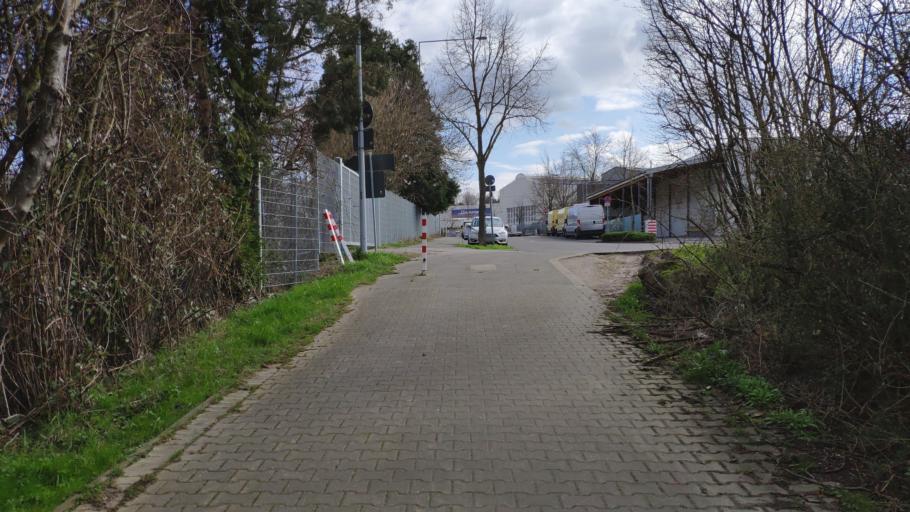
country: DE
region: North Rhine-Westphalia
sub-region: Regierungsbezirk Koln
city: Wurselen
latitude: 50.7910
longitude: 6.1374
